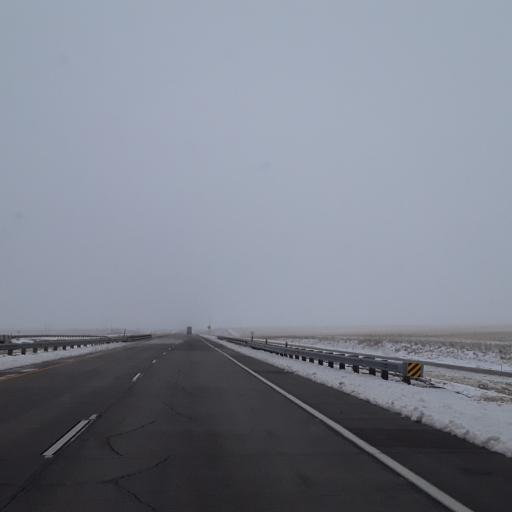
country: US
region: Colorado
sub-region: Logan County
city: Sterling
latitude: 40.7076
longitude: -103.0565
